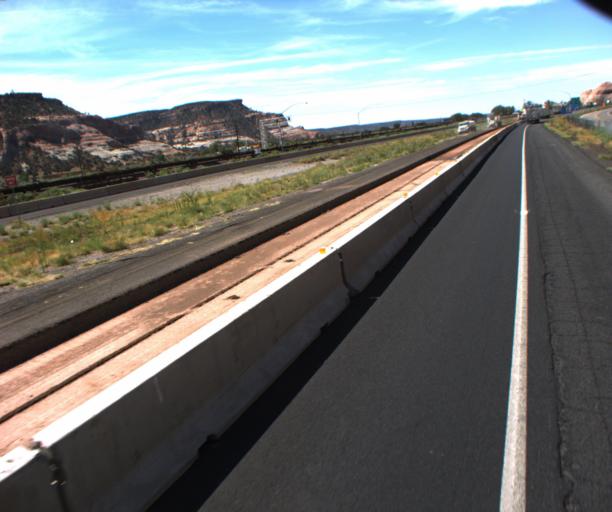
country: US
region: Arizona
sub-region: Apache County
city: Houck
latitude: 35.3625
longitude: -109.0472
